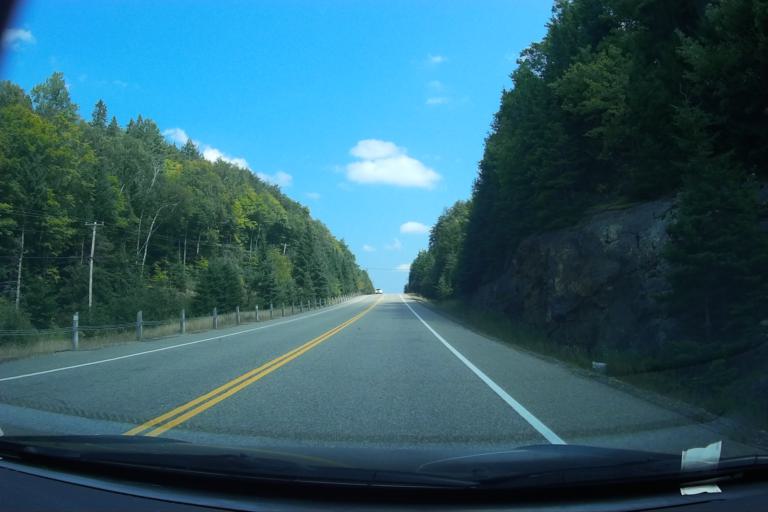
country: CA
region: Ontario
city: Huntsville
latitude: 45.5653
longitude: -78.5416
